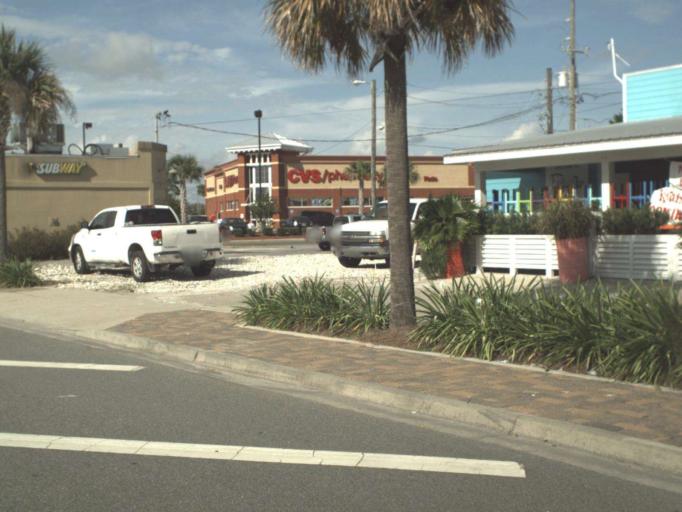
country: US
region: Florida
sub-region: Gulf County
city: Port Saint Joe
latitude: 29.8152
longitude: -85.3047
